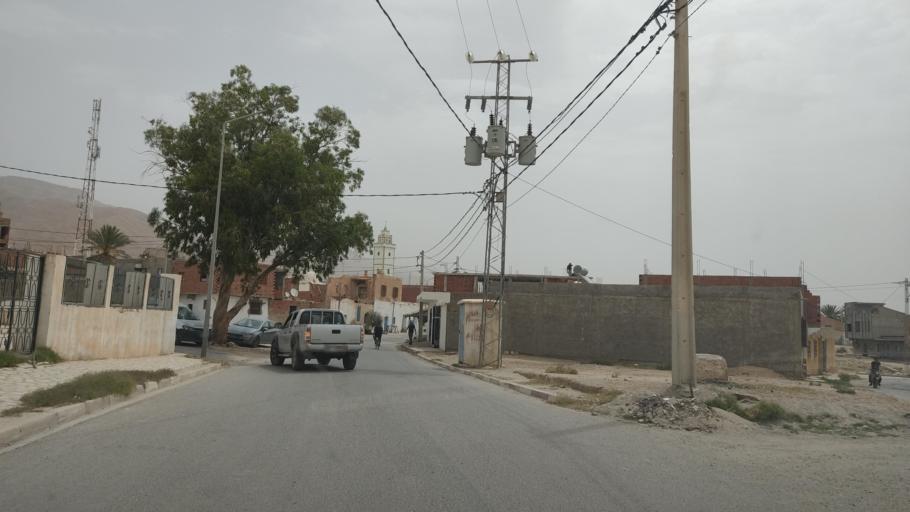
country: TN
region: Gafsa
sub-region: Gafsa Municipality
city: Gafsa
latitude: 34.3338
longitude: 8.9503
